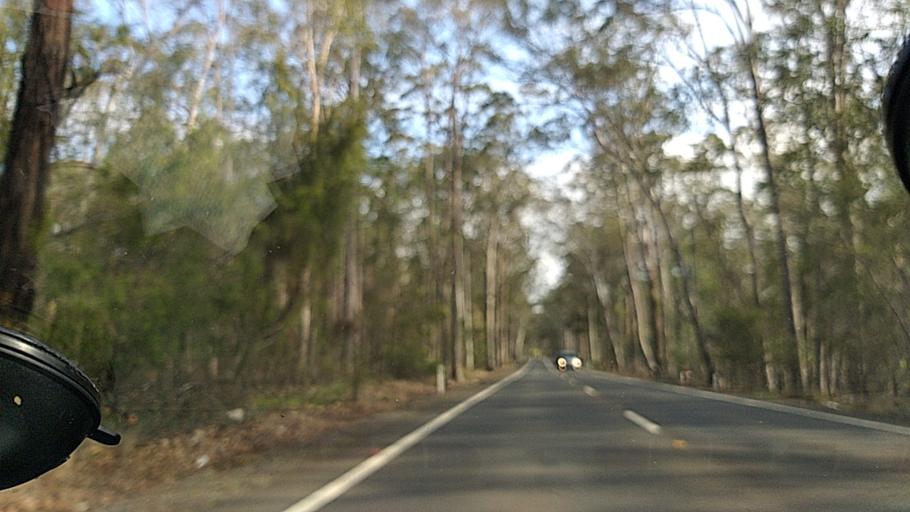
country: AU
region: New South Wales
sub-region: Campbelltown Municipality
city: Glen Alpine
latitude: -34.1420
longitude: 150.7907
